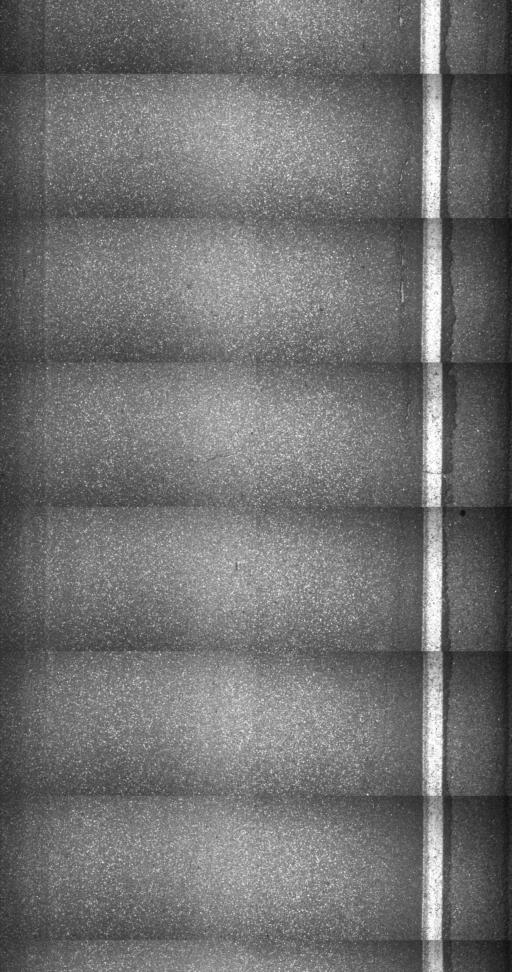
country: US
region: Vermont
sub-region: Caledonia County
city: Hardwick
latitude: 44.5284
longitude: -72.4218
